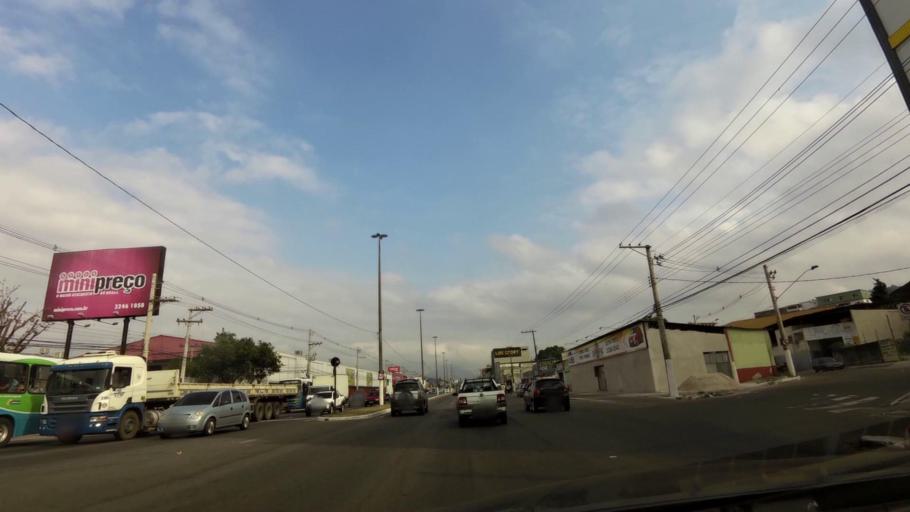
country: BR
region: Espirito Santo
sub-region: Vitoria
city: Vitoria
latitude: -20.3543
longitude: -40.3411
